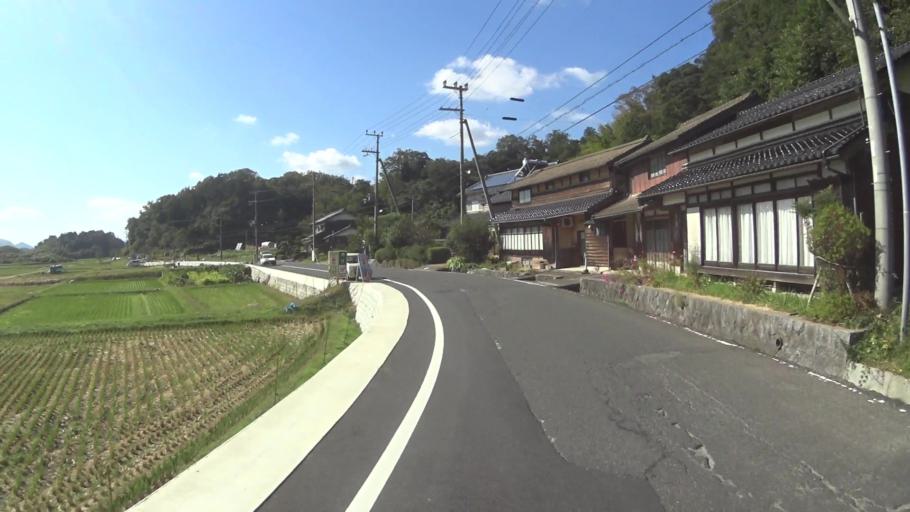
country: JP
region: Kyoto
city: Miyazu
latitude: 35.6889
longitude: 135.0942
